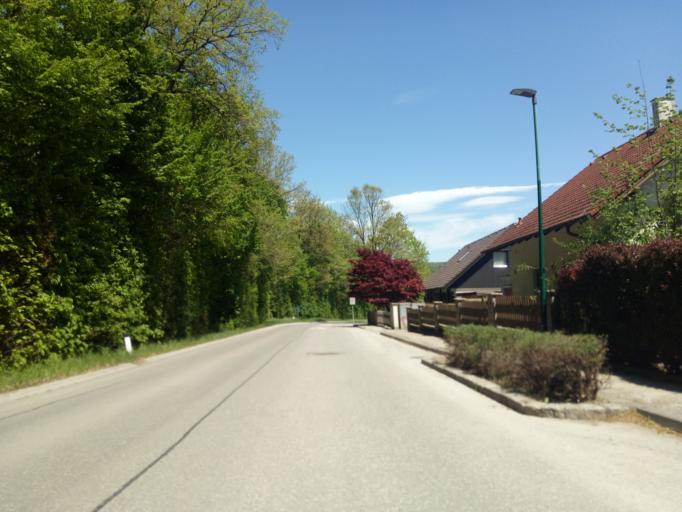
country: AT
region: Lower Austria
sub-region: Politischer Bezirk Modling
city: Kaltenleutgeben
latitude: 48.1310
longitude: 16.1933
